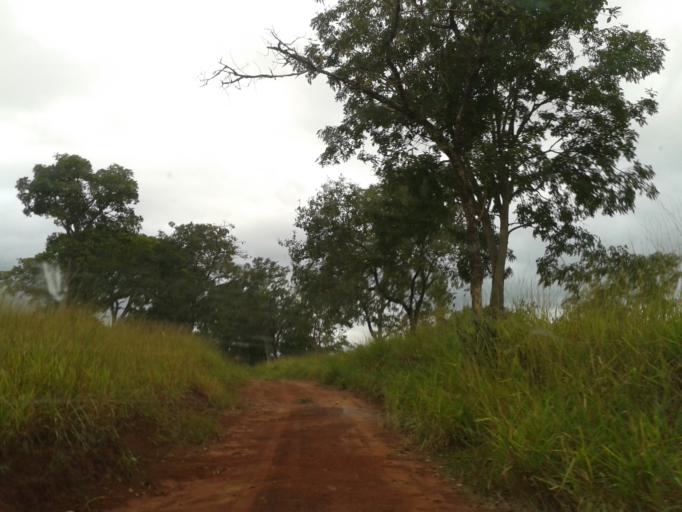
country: BR
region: Minas Gerais
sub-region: Campina Verde
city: Campina Verde
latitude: -19.4886
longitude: -49.6294
